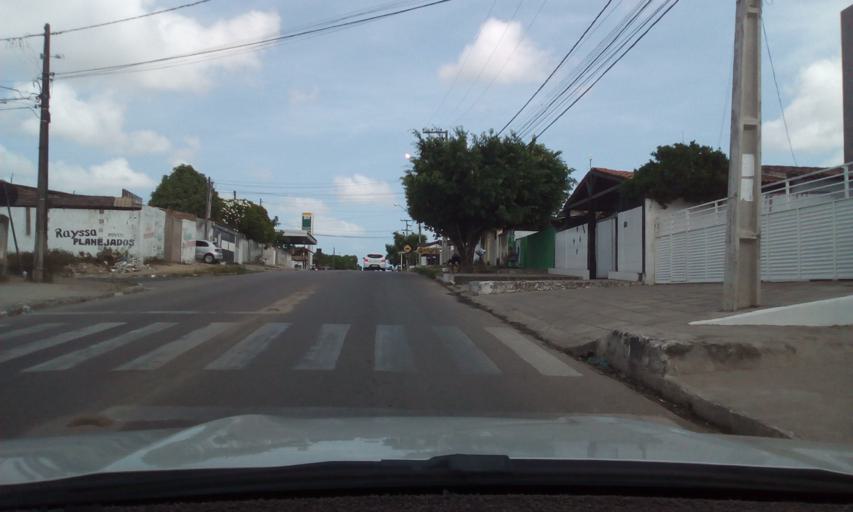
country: BR
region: Paraiba
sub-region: Joao Pessoa
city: Joao Pessoa
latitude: -7.1772
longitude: -34.8810
